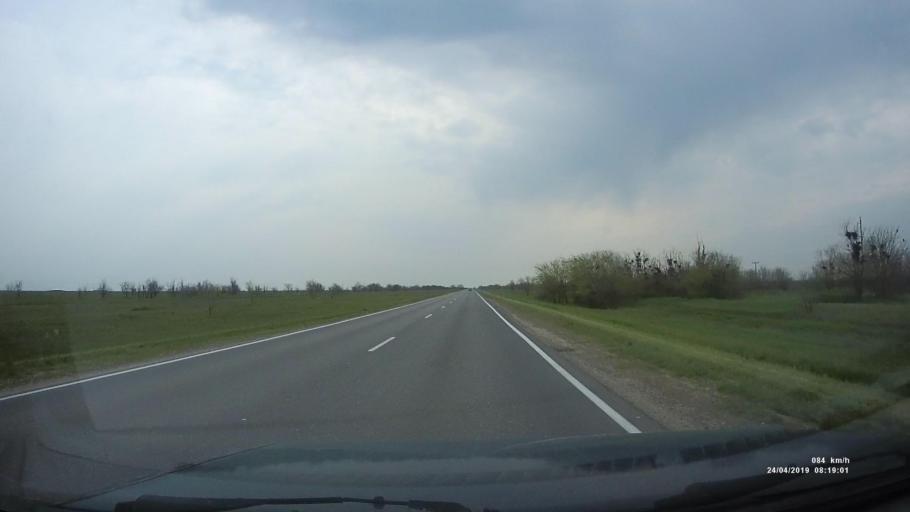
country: RU
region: Kalmykiya
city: Priyutnoye
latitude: 46.1020
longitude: 43.6570
